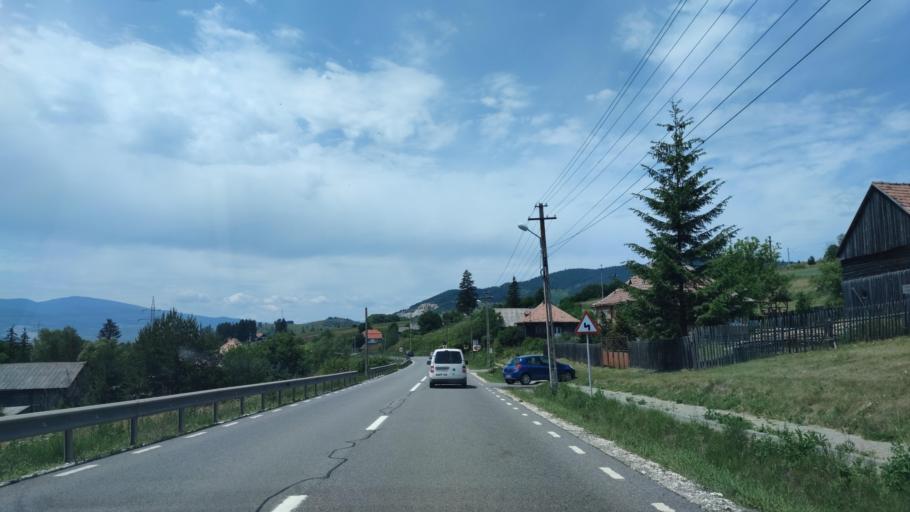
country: RO
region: Harghita
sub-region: Comuna Voslobeni
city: Voslobeni
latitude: 46.6277
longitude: 25.6753
